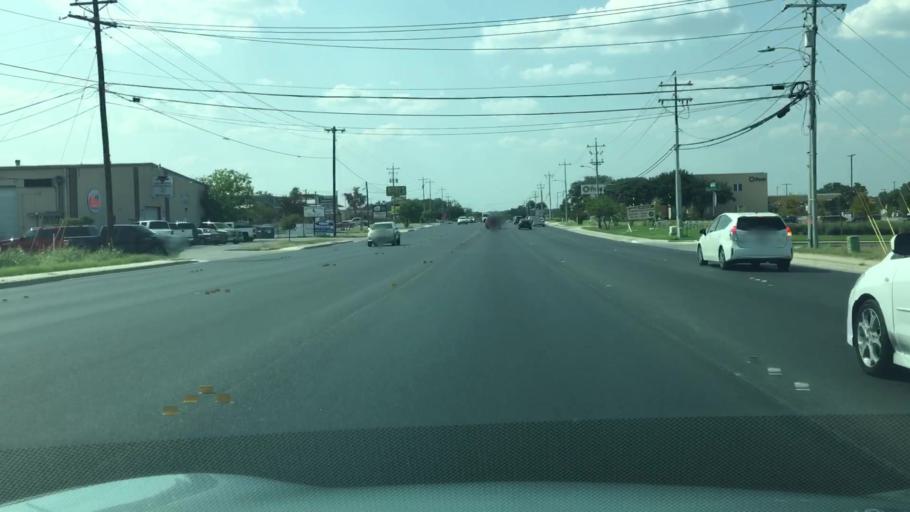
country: US
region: Texas
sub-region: Hays County
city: San Marcos
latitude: 29.8626
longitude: -97.9596
